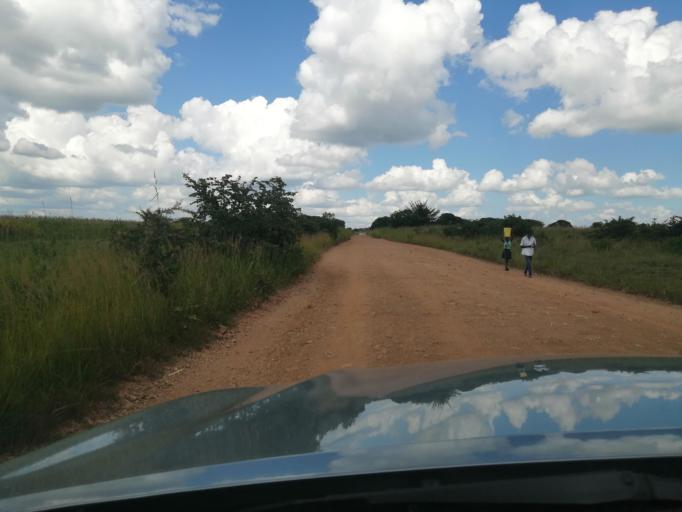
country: ZM
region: Lusaka
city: Lusaka
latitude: -15.1995
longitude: 28.0351
